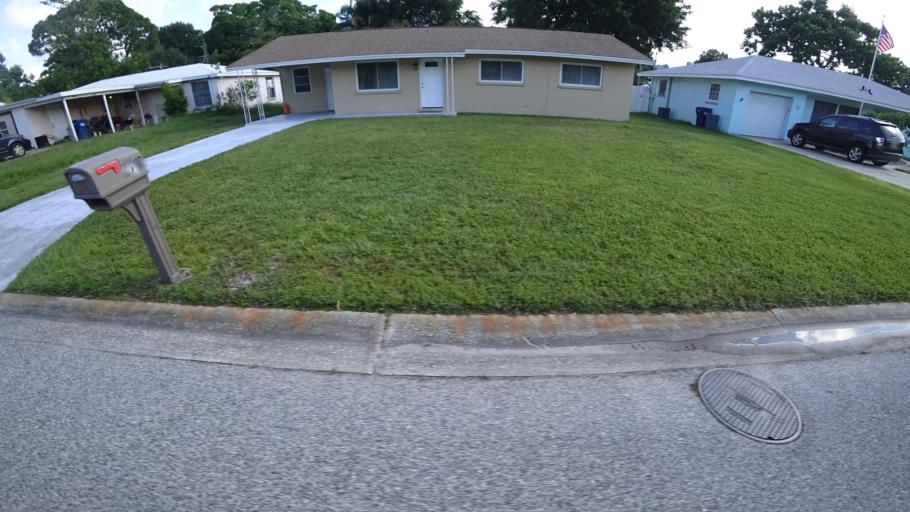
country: US
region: Florida
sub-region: Manatee County
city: South Bradenton
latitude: 27.4657
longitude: -82.5893
